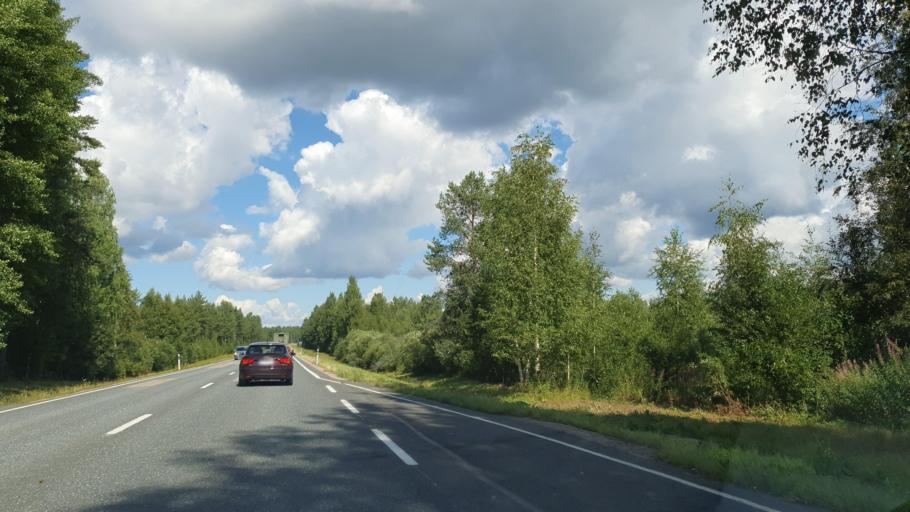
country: FI
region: Kainuu
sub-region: Kajaani
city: Kajaani
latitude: 64.1095
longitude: 27.4482
